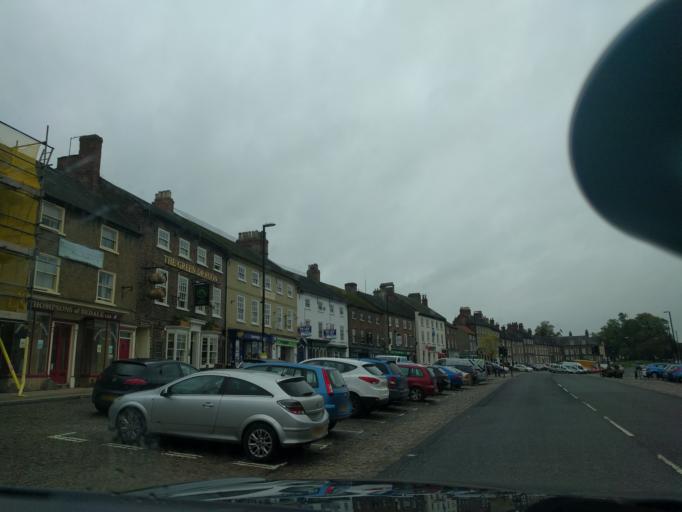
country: GB
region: England
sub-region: North Yorkshire
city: Bedale
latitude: 54.2886
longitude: -1.5922
